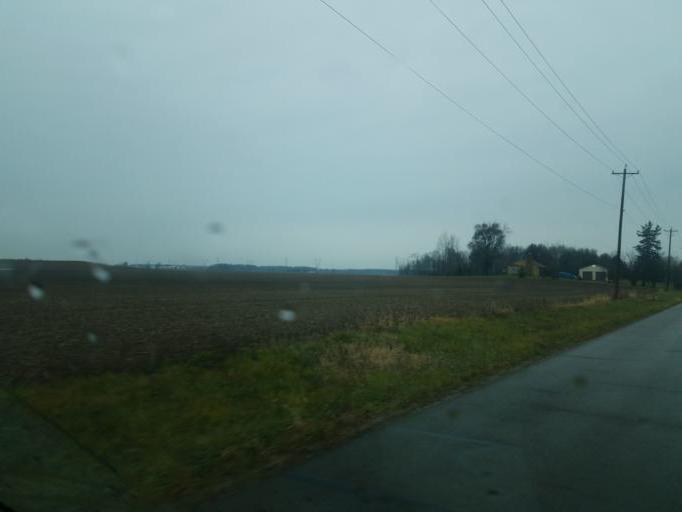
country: US
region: Ohio
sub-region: Knox County
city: Centerburg
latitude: 40.2617
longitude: -82.7182
